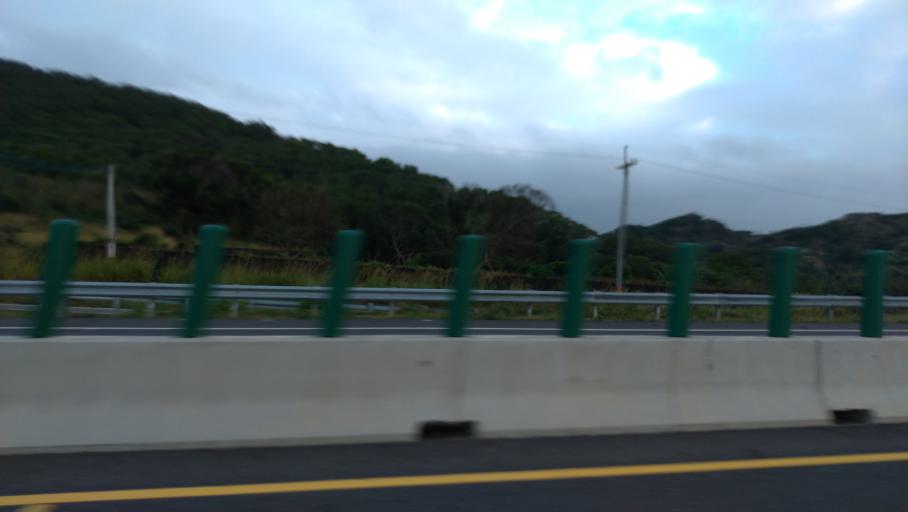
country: TW
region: Taiwan
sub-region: Miaoli
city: Miaoli
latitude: 24.5334
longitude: 120.6971
